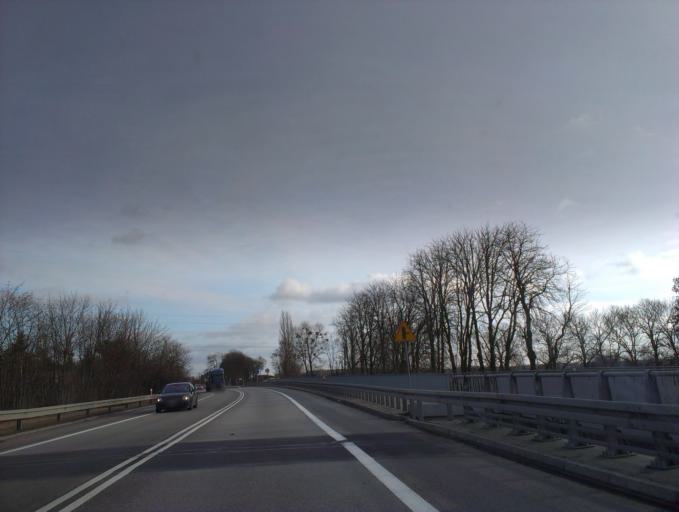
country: PL
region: Kujawsko-Pomorskie
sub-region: Powiat lipnowski
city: Lipno
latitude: 52.8542
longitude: 19.1645
